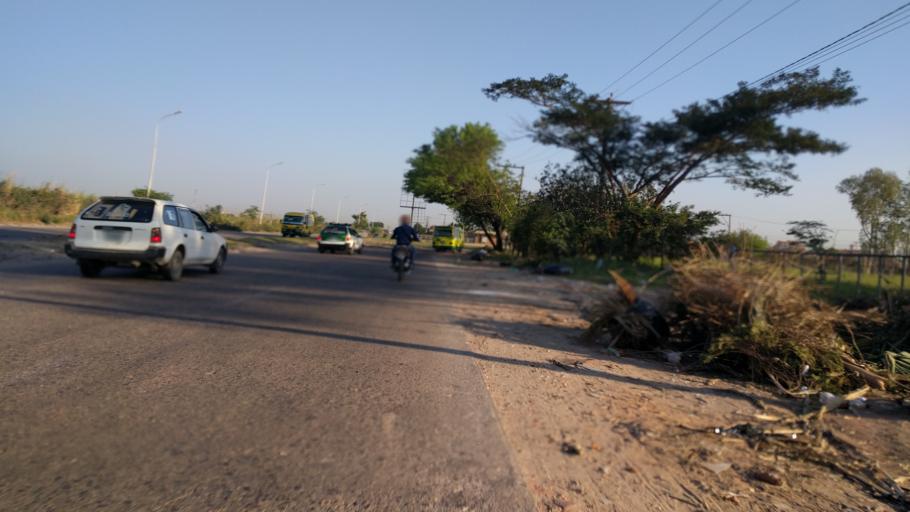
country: BO
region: Santa Cruz
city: Santa Cruz de la Sierra
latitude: -17.8171
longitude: -63.1658
